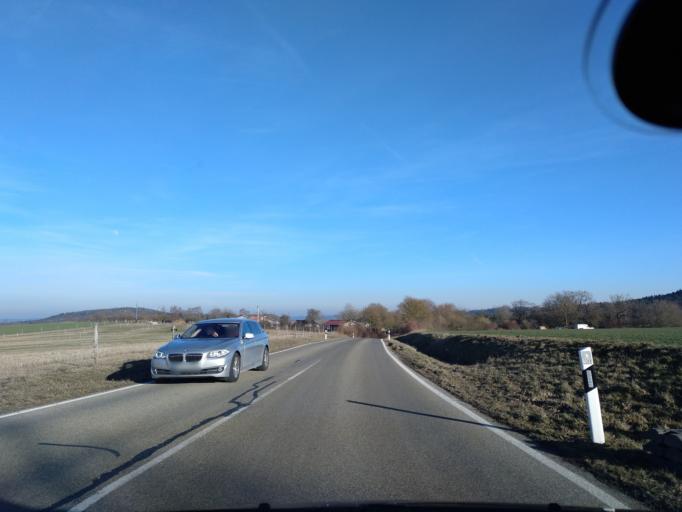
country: DE
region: Baden-Wuerttemberg
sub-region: Regierungsbezirk Stuttgart
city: Rosenberg
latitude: 49.0729
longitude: 9.9763
